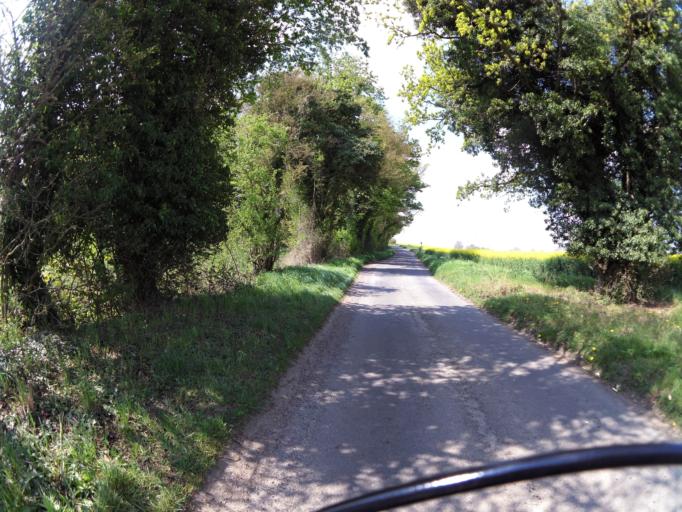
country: GB
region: England
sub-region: Suffolk
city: Bramford
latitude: 52.0818
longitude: 1.0736
